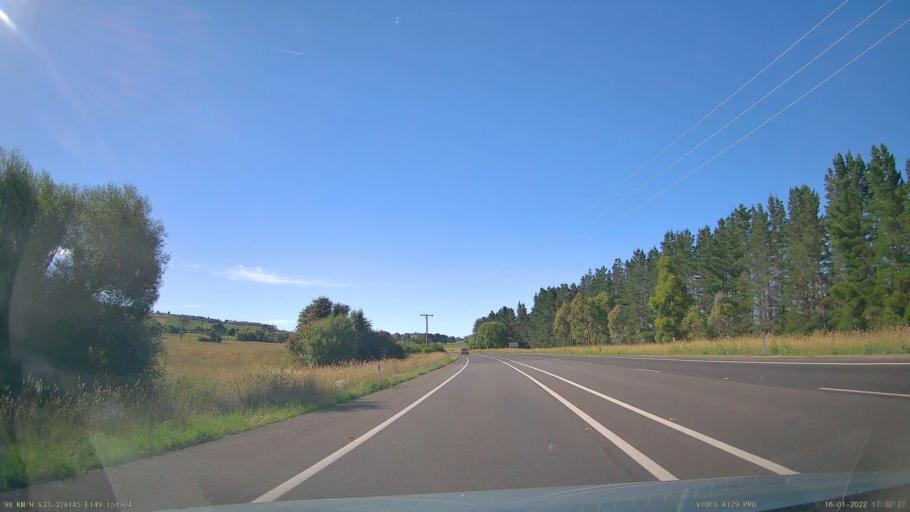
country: AU
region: New South Wales
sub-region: Orange Municipality
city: Orange
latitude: -33.3279
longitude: 149.1518
